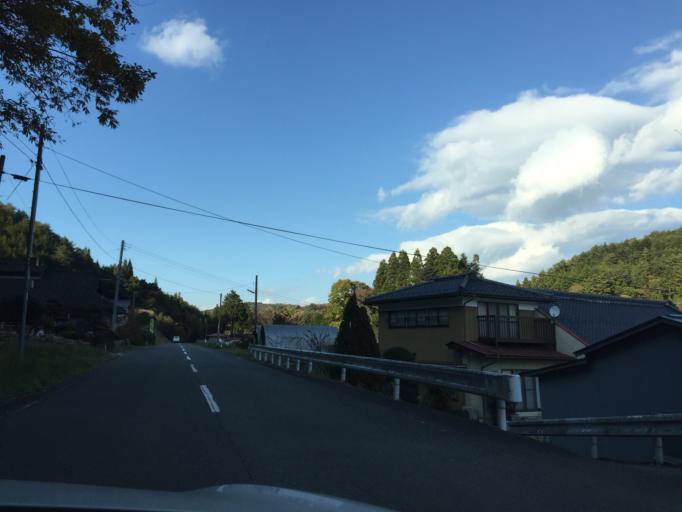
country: JP
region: Fukushima
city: Iwaki
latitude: 37.2631
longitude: 140.7648
